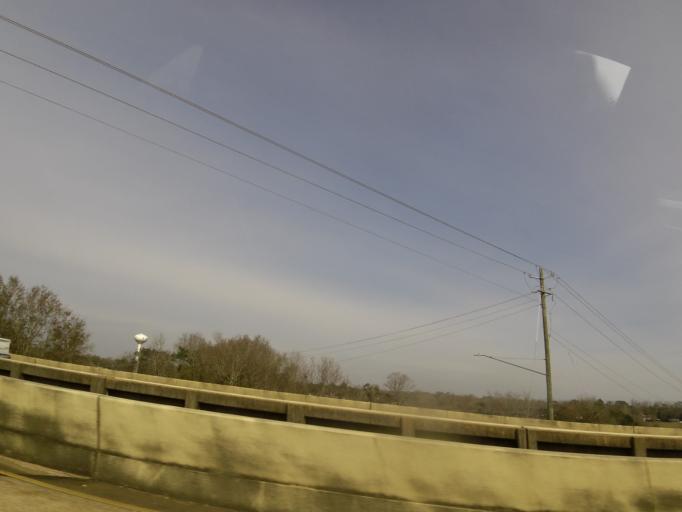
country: US
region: Alabama
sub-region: Dale County
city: Midland City
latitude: 31.3137
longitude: -85.5061
